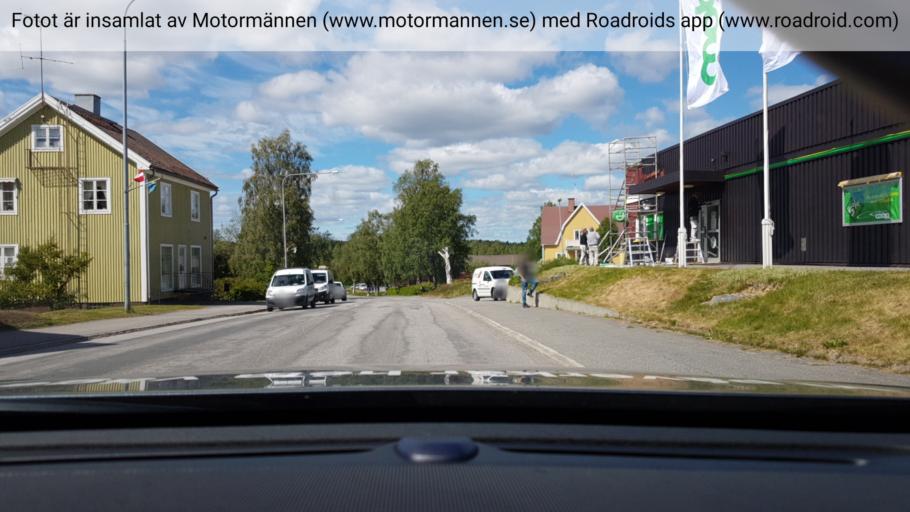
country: SE
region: Vaesterbotten
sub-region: Skelleftea Kommun
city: Burea
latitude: 64.3702
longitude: 21.3118
